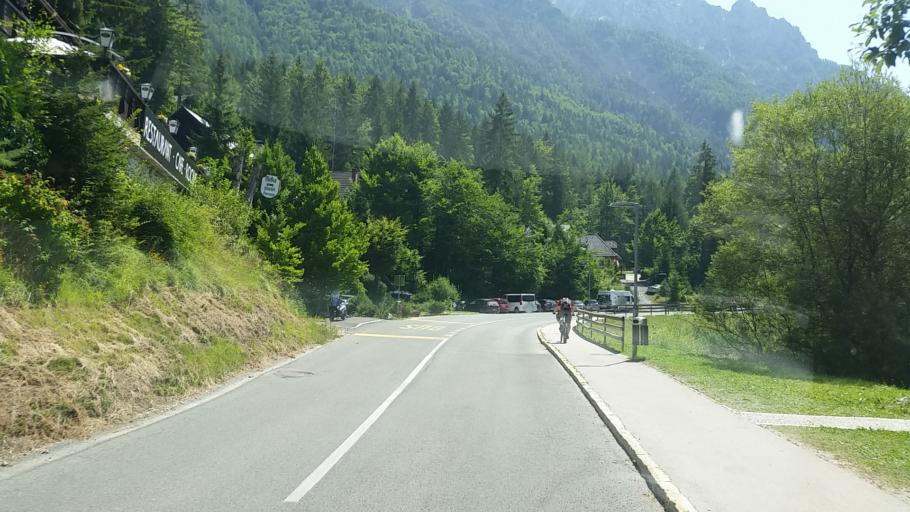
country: SI
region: Kranjska Gora
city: Kranjska Gora
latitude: 46.4751
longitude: 13.7845
